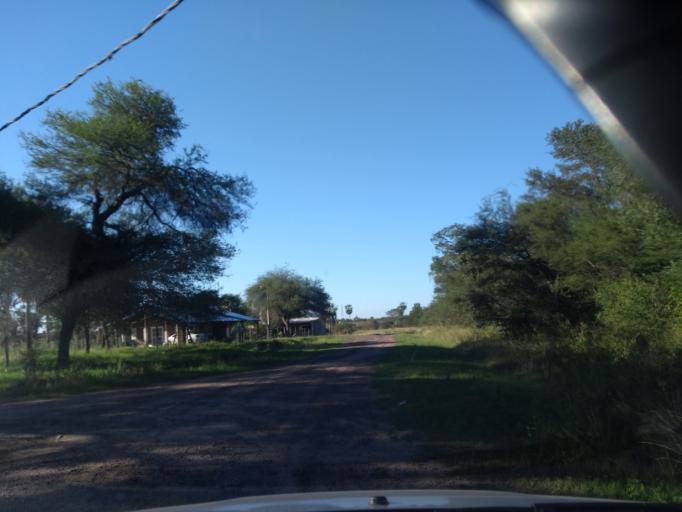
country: AR
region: Chaco
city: Barranqueras
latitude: -27.4406
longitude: -58.9034
